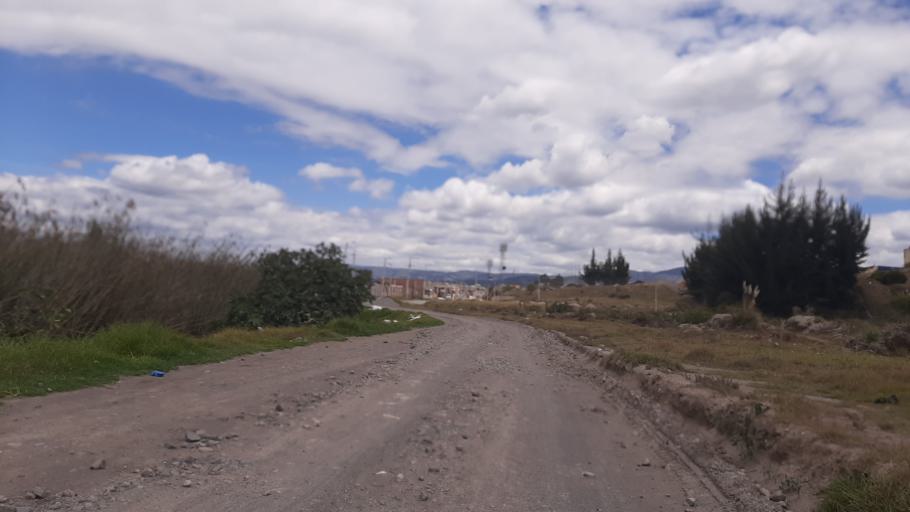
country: EC
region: Chimborazo
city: Riobamba
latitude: -1.6505
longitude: -78.6397
